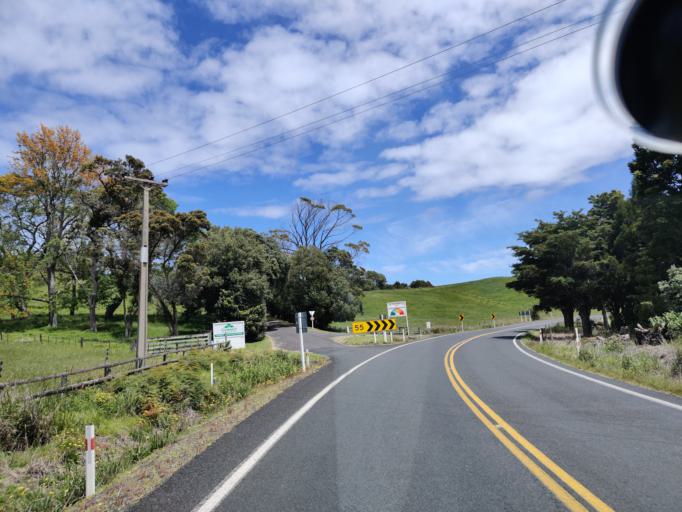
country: NZ
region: Northland
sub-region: Far North District
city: Kaitaia
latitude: -35.0100
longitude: 173.2000
